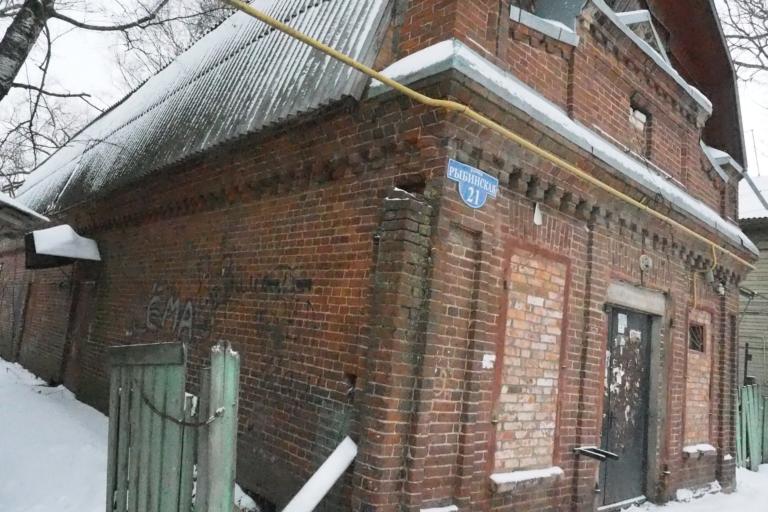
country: RU
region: Tverskaya
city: Bezhetsk
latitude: 57.7821
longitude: 36.6995
